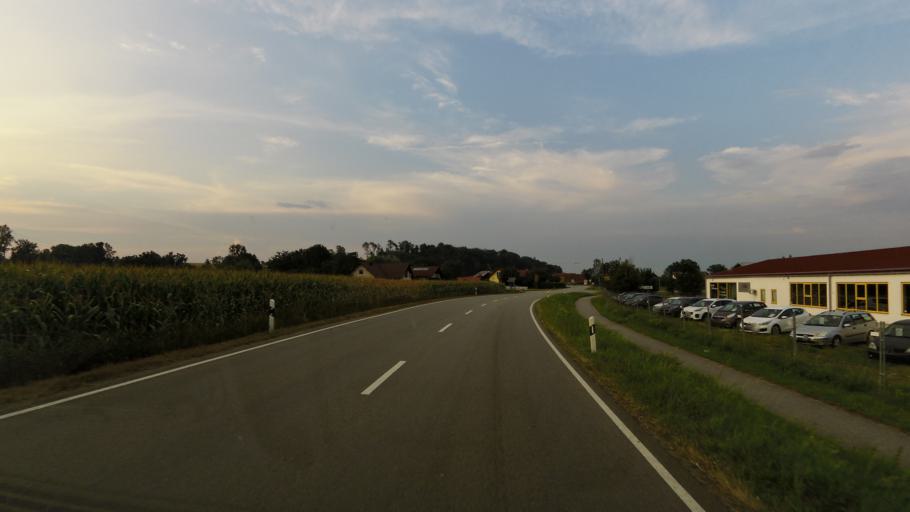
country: DE
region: Bavaria
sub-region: Lower Bavaria
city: Kirchham
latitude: 48.3472
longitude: 13.2469
